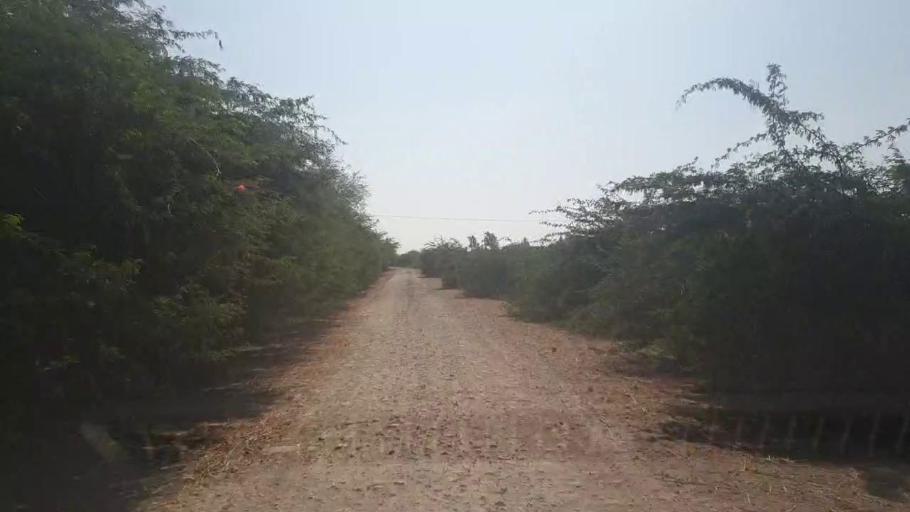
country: PK
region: Sindh
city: Badin
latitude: 24.5810
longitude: 68.8464
